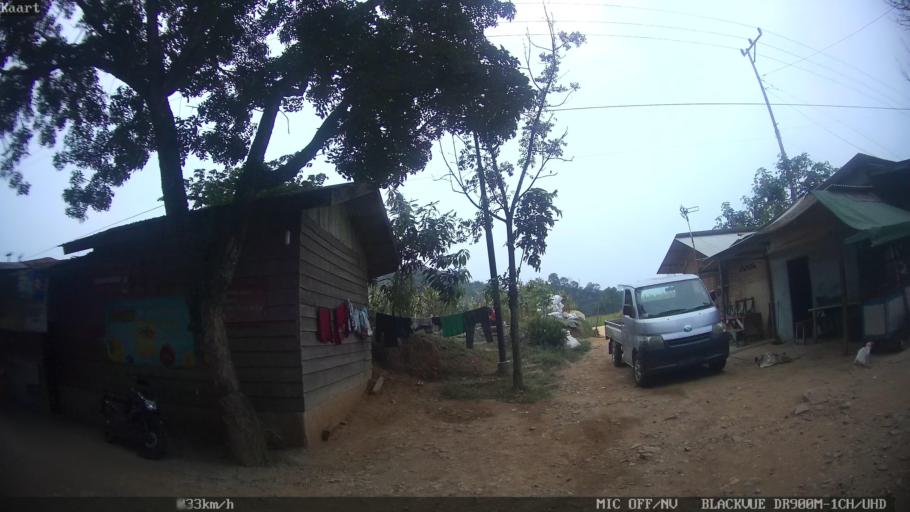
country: ID
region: Lampung
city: Panjang
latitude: -5.4208
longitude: 105.3342
